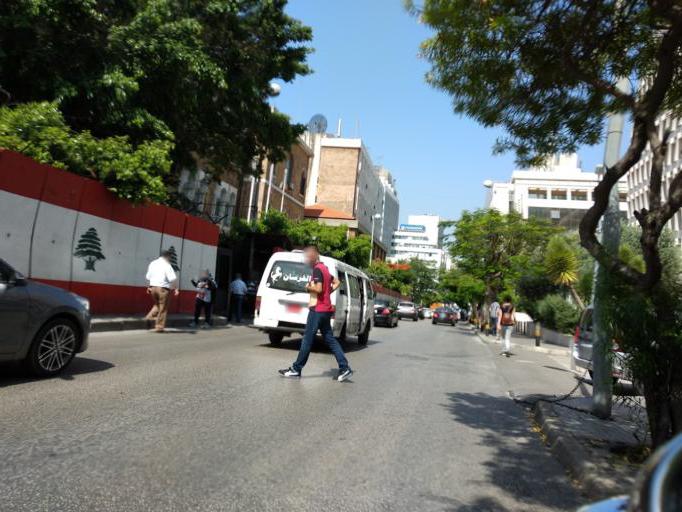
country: LB
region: Beyrouth
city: Ra's Bayrut
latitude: 33.8953
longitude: 35.4895
